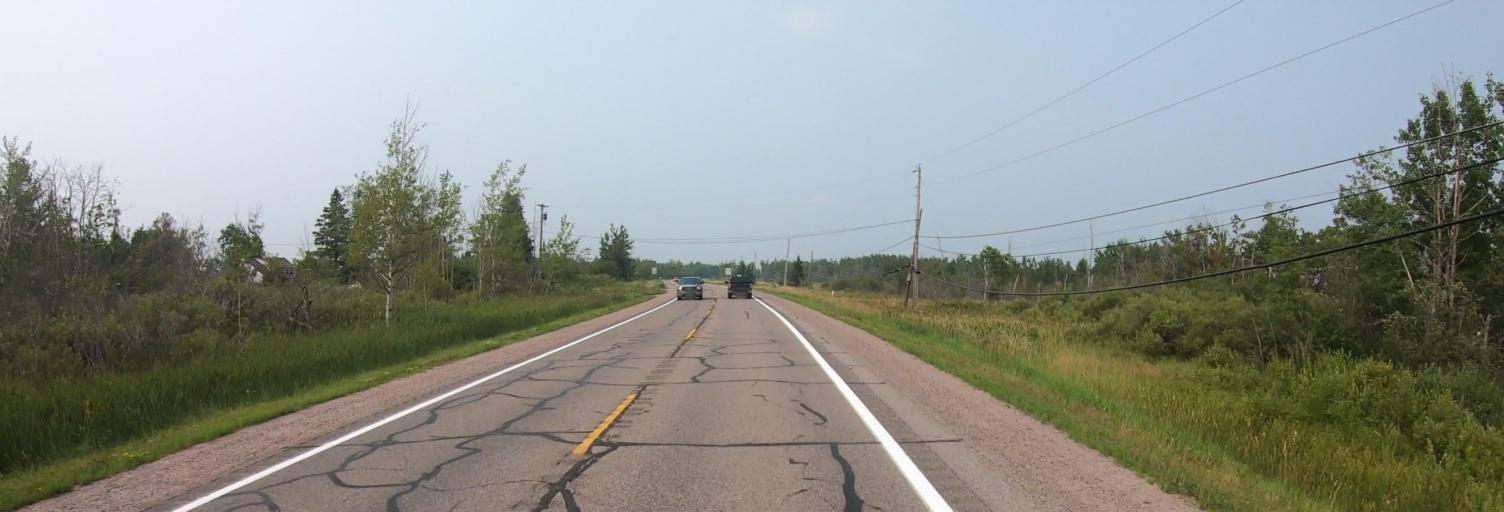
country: US
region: Michigan
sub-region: Chippewa County
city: Sault Ste. Marie
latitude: 46.4473
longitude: -84.3536
